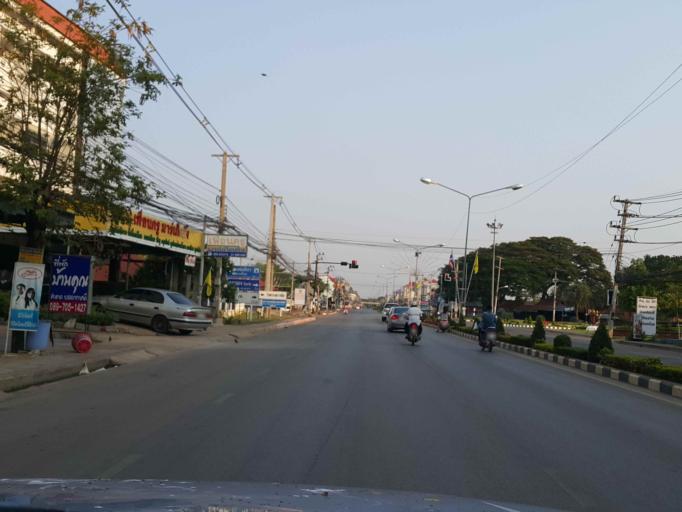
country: TH
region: Sukhothai
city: Sawankhalok
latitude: 17.3039
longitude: 99.8335
